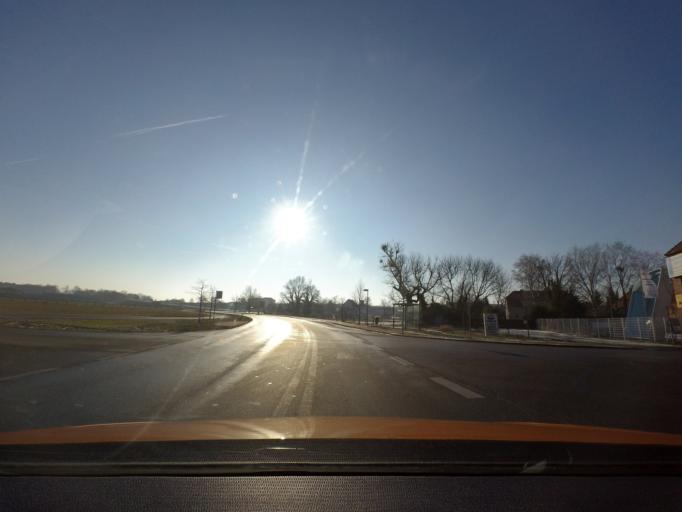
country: DE
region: Brandenburg
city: Falkensee
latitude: 52.5355
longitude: 13.0862
